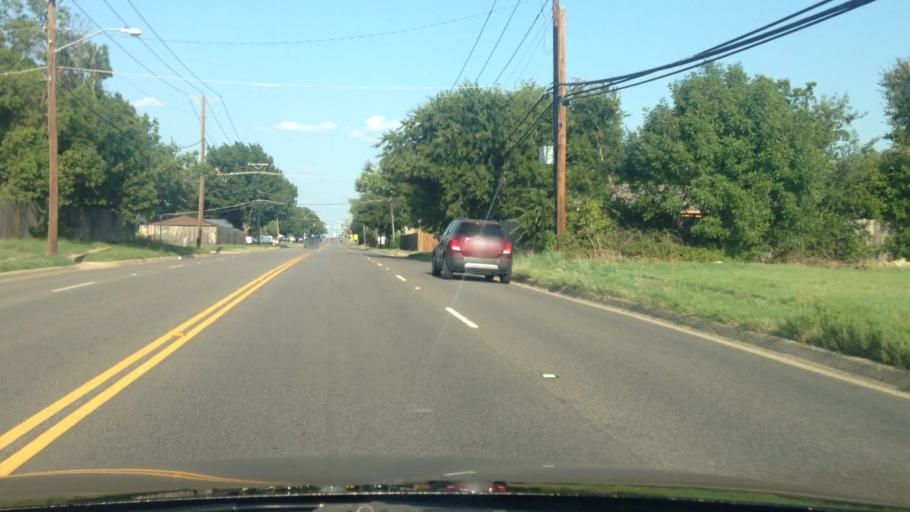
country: US
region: Texas
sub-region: Tarrant County
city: Edgecliff Village
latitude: 32.6351
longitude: -97.3310
